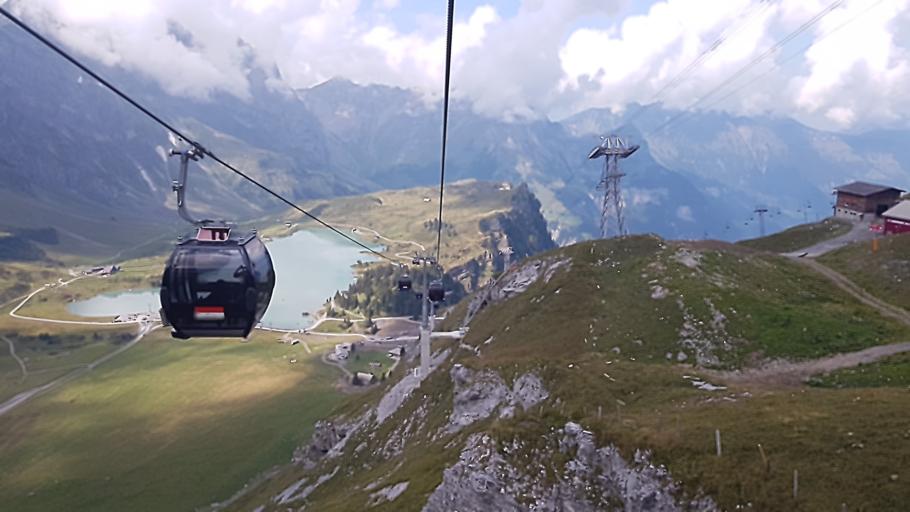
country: CH
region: Obwalden
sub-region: Obwalden
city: Engelberg
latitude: 46.7878
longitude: 8.4075
